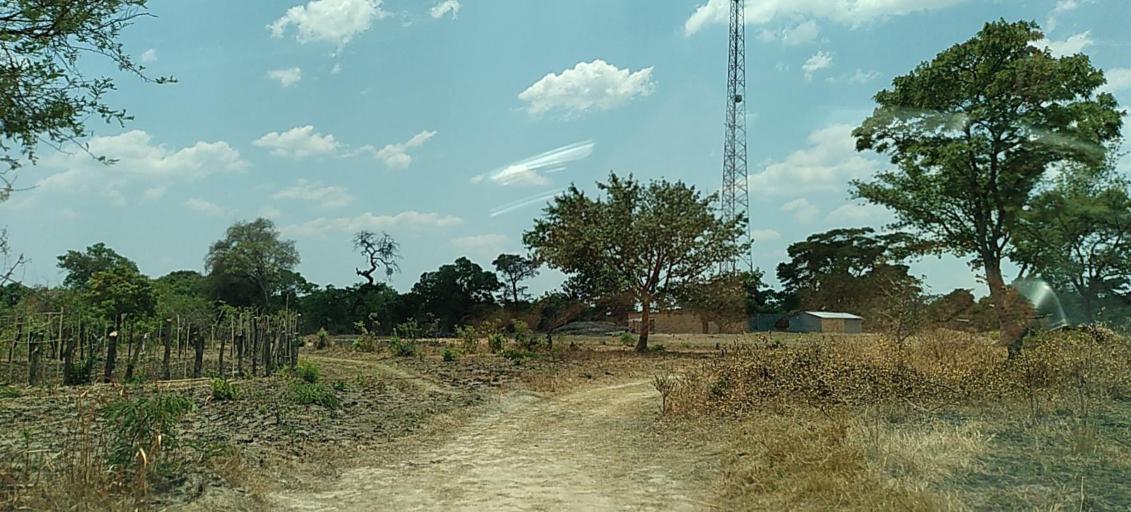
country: ZM
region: Copperbelt
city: Chililabombwe
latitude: -12.4495
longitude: 27.6795
